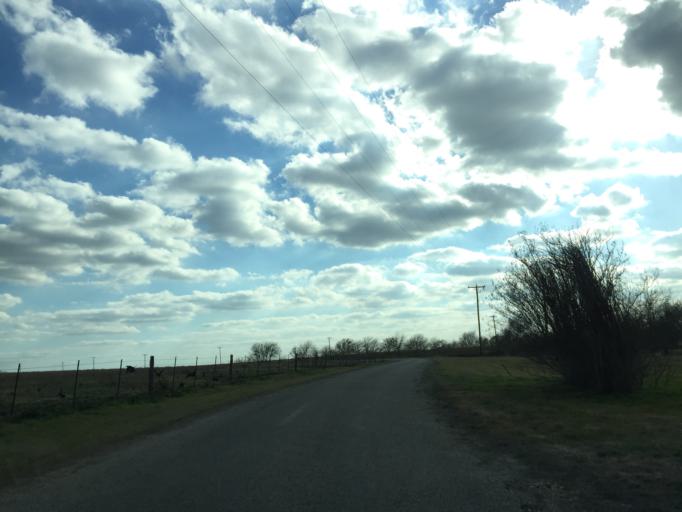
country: US
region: Texas
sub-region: Williamson County
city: Taylor
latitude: 30.6313
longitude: -97.4353
